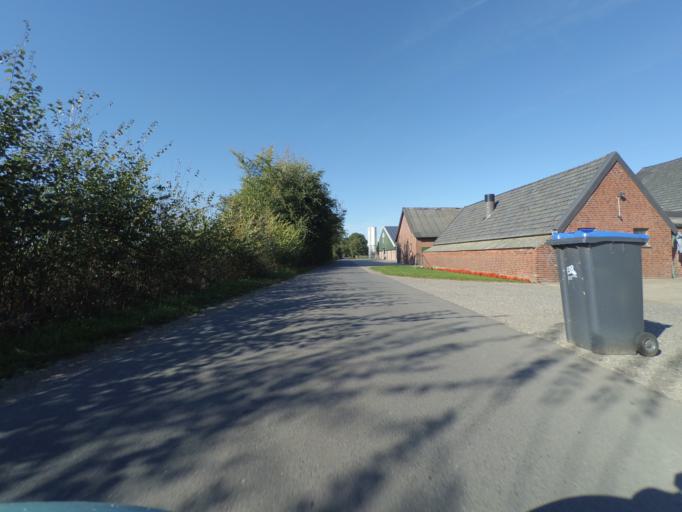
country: DE
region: North Rhine-Westphalia
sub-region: Regierungsbezirk Dusseldorf
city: Bocholt
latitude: 51.8175
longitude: 6.5589
